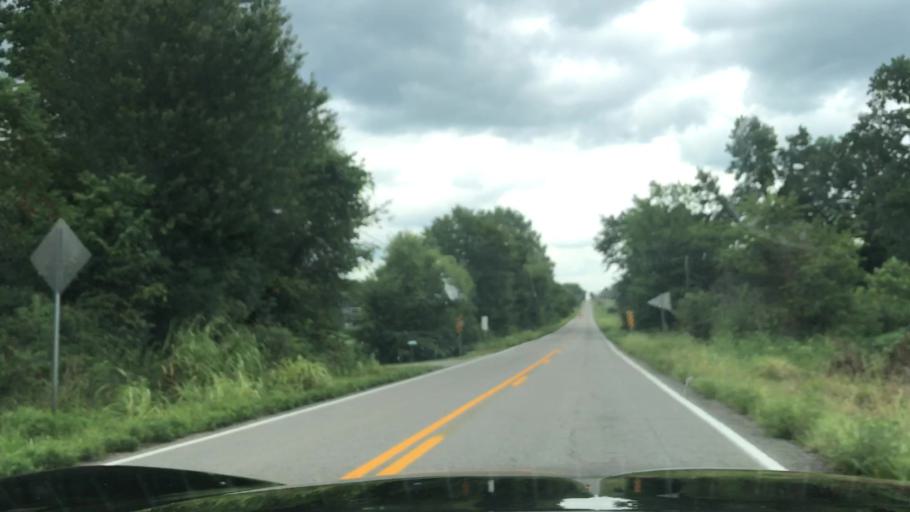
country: US
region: Kentucky
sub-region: Muhlenberg County
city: Central City
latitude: 37.1959
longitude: -86.9859
